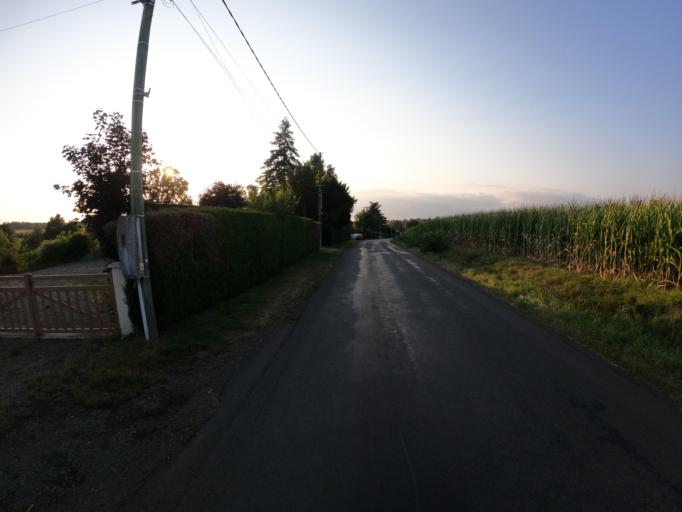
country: FR
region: Pays de la Loire
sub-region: Departement de la Sarthe
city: Parce-sur-Sarthe
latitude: 47.8551
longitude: -0.1944
